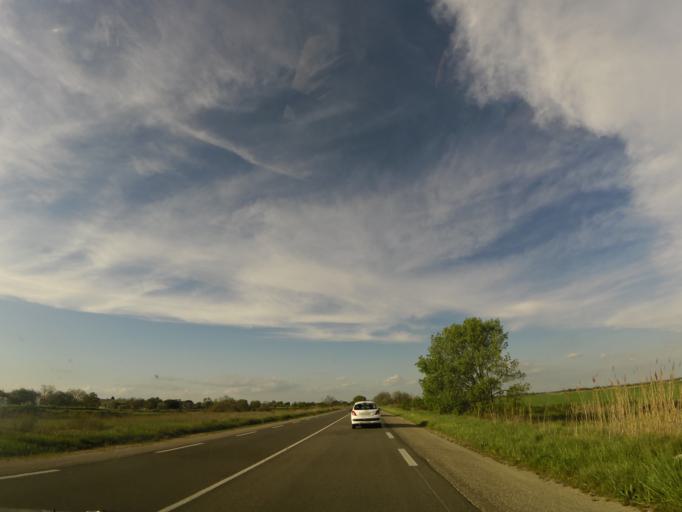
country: FR
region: Languedoc-Roussillon
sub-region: Departement de l'Herault
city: La Grande-Motte
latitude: 43.6006
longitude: 4.1058
